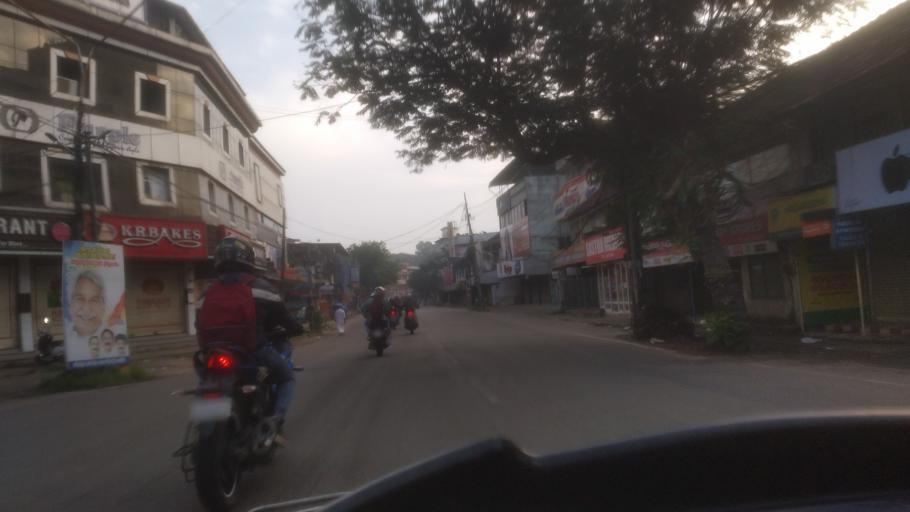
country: IN
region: Kerala
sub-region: Ernakulam
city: Aluva
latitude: 10.1119
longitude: 76.3523
